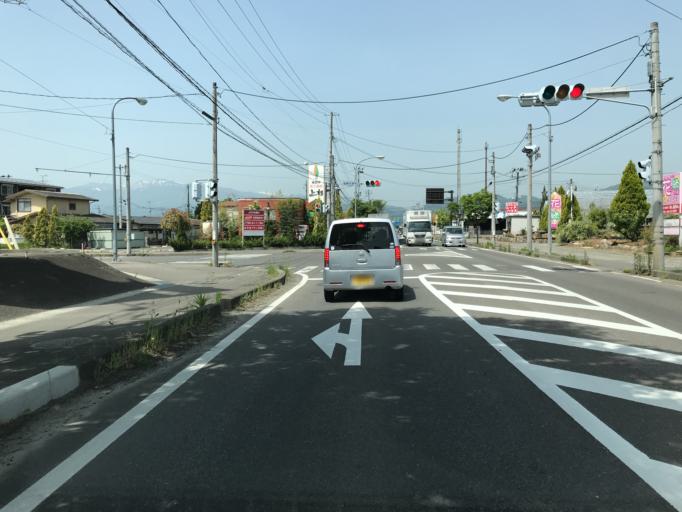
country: JP
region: Fukushima
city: Fukushima-shi
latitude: 37.7940
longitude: 140.4458
